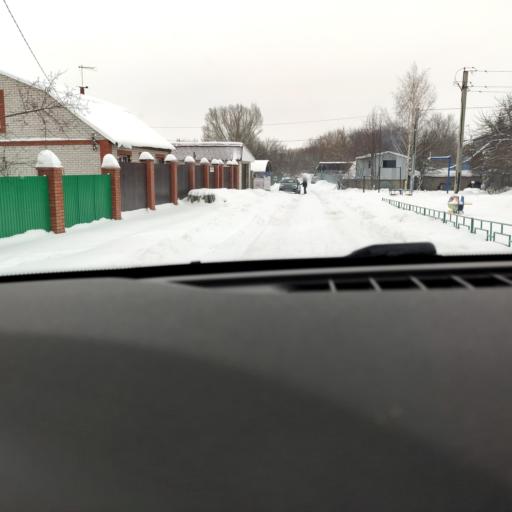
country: RU
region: Samara
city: Smyshlyayevka
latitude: 53.2419
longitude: 50.3466
